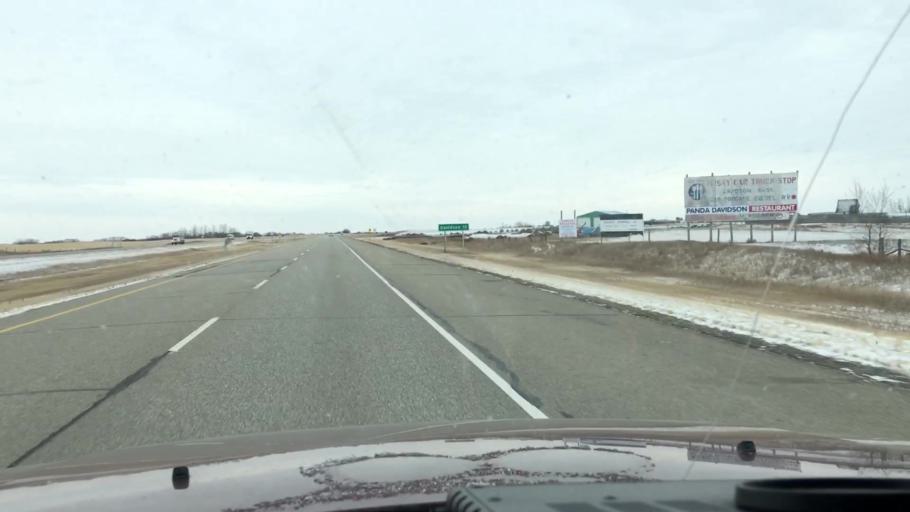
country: CA
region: Saskatchewan
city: Watrous
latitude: 51.3677
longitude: -106.1337
